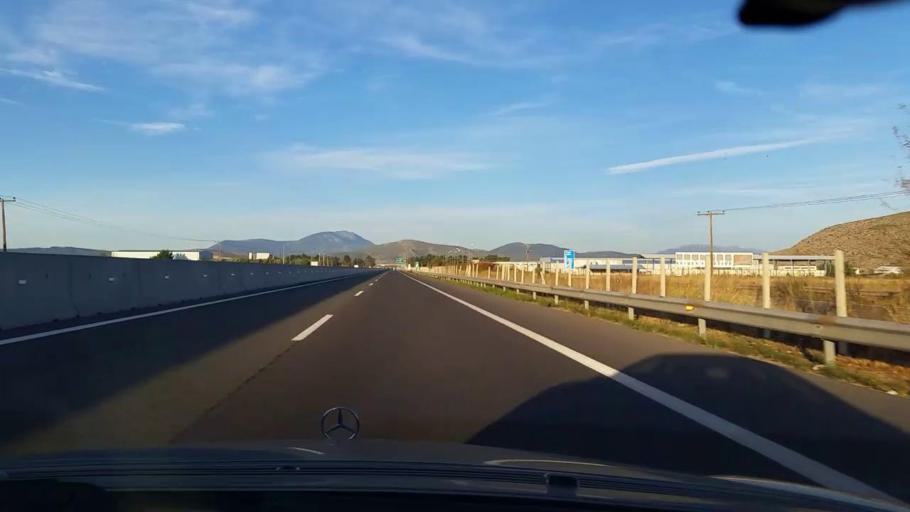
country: GR
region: Central Greece
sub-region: Nomos Voiotias
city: Thivai
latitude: 38.3662
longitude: 23.3342
